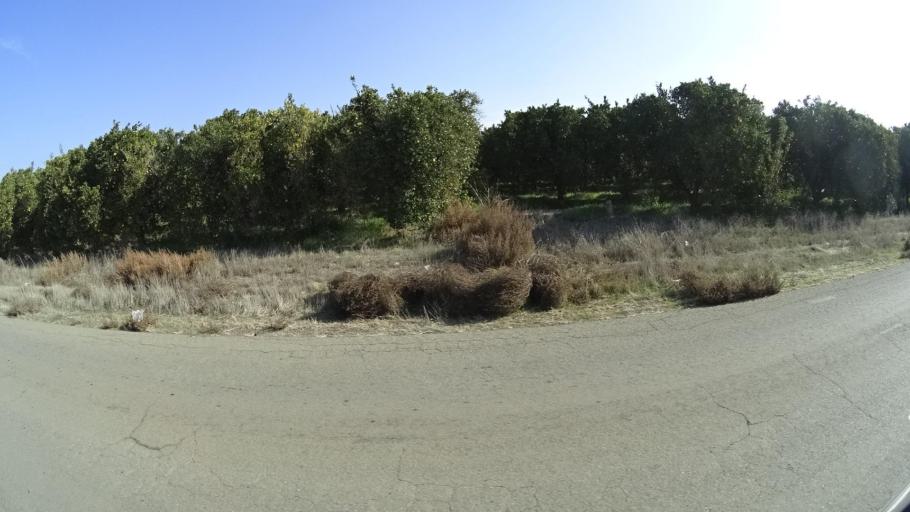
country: US
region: California
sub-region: Kern County
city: McFarland
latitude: 35.6416
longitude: -119.1690
